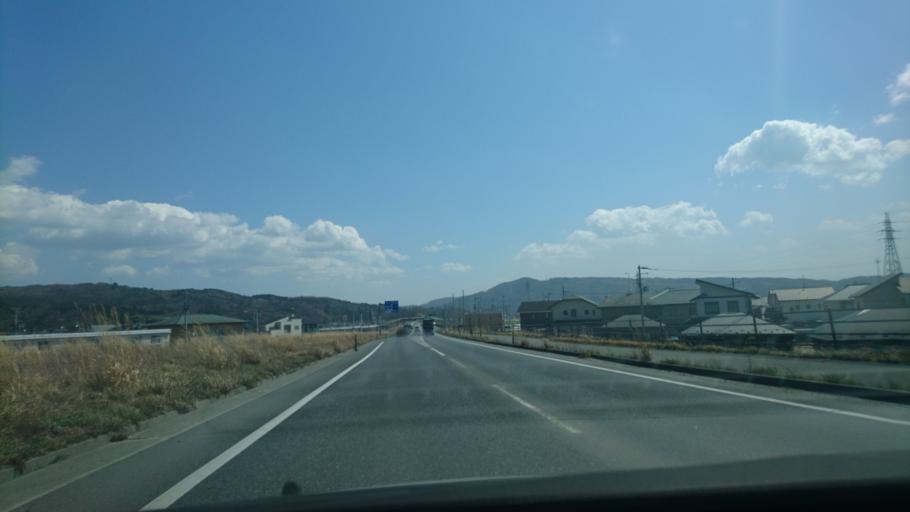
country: JP
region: Miyagi
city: Ishinomaki
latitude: 38.4563
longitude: 141.2994
